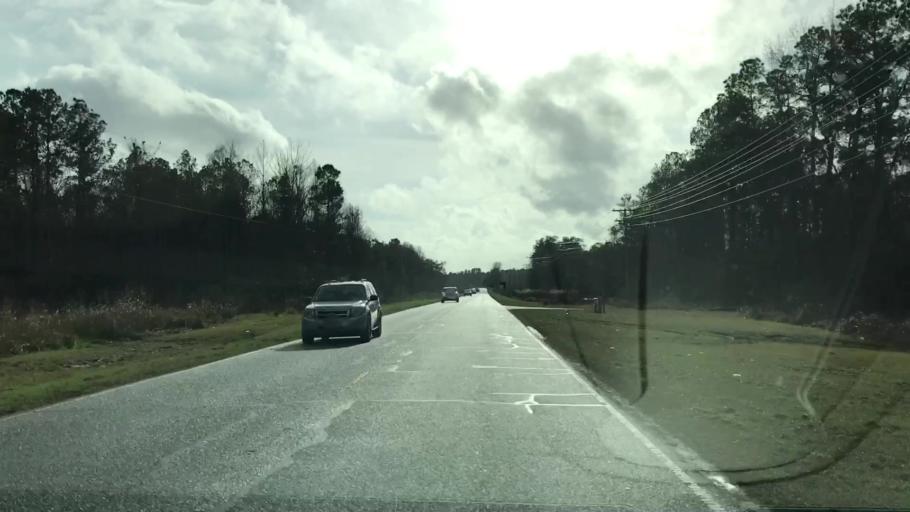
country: US
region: South Carolina
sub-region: Williamsburg County
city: Andrews
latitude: 33.4791
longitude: -79.5559
